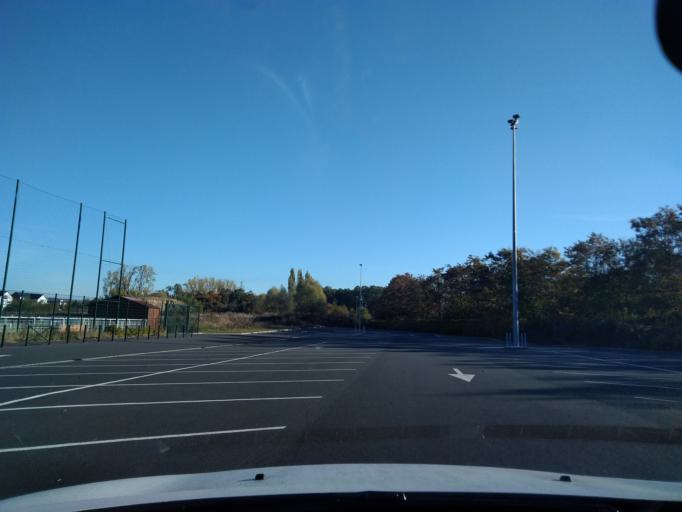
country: FR
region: Lorraine
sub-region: Departement de la Moselle
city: Sarreguemines
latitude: 49.1063
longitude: 7.0836
